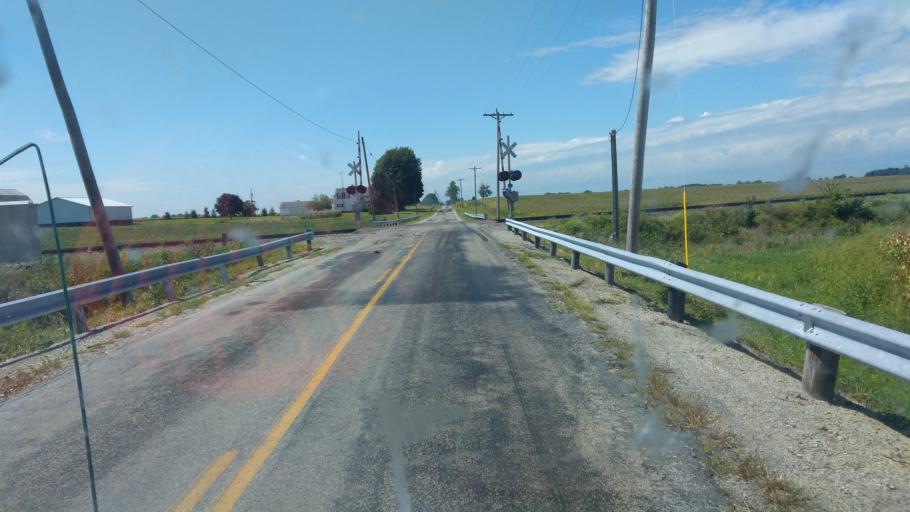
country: US
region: Ohio
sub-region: Marion County
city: Marion
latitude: 40.6587
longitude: -83.1912
